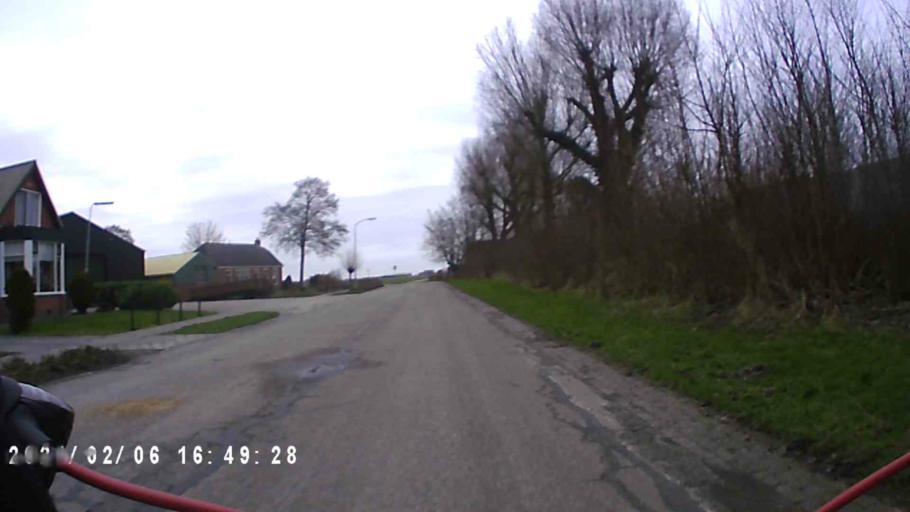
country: NL
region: Groningen
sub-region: Gemeente Appingedam
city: Appingedam
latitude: 53.4140
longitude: 6.7350
